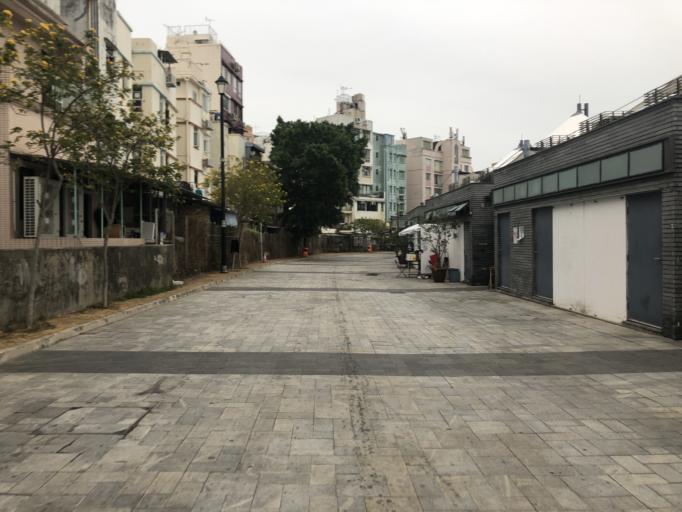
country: HK
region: Wanchai
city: Wan Chai
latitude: 22.2182
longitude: 114.2121
